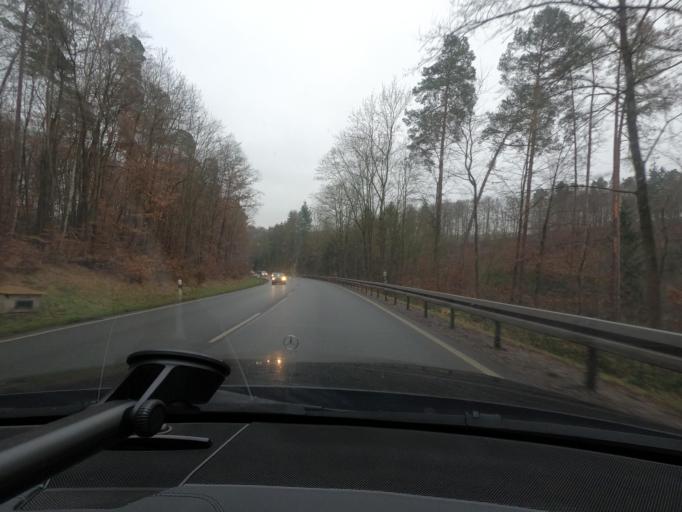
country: DE
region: Hesse
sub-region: Regierungsbezirk Kassel
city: Bad Arolsen
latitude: 51.3515
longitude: 9.0771
